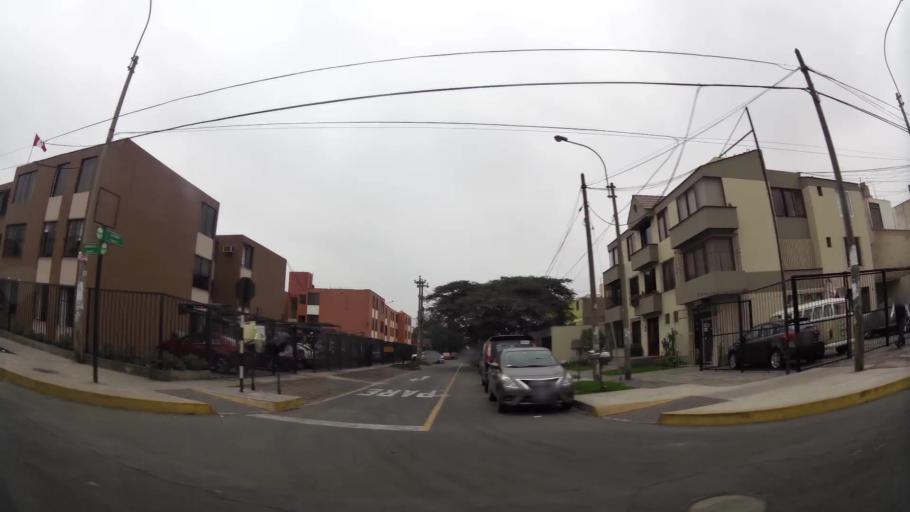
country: PE
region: Lima
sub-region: Lima
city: La Molina
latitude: -12.0986
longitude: -76.9489
